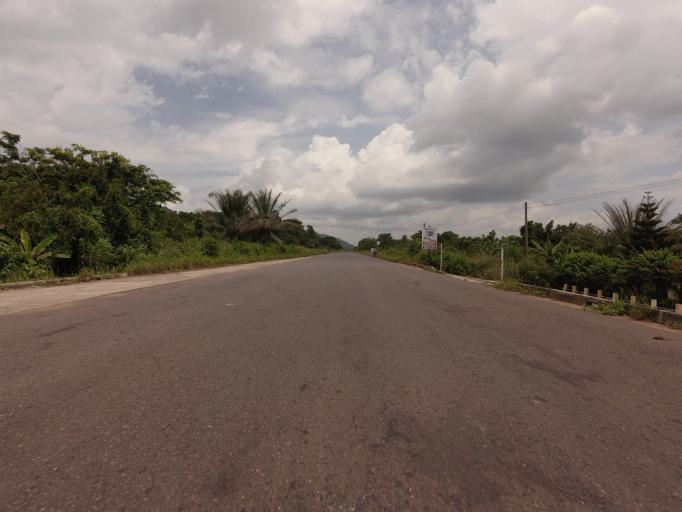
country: GH
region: Volta
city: Ho
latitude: 6.4959
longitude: 0.2030
